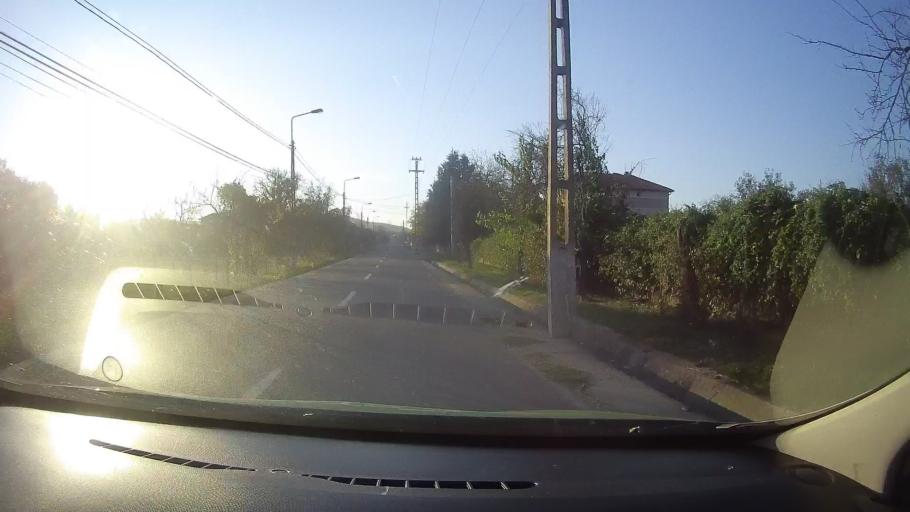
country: RO
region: Timis
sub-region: Comuna Fardea
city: Fardea
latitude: 45.7415
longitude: 22.1639
